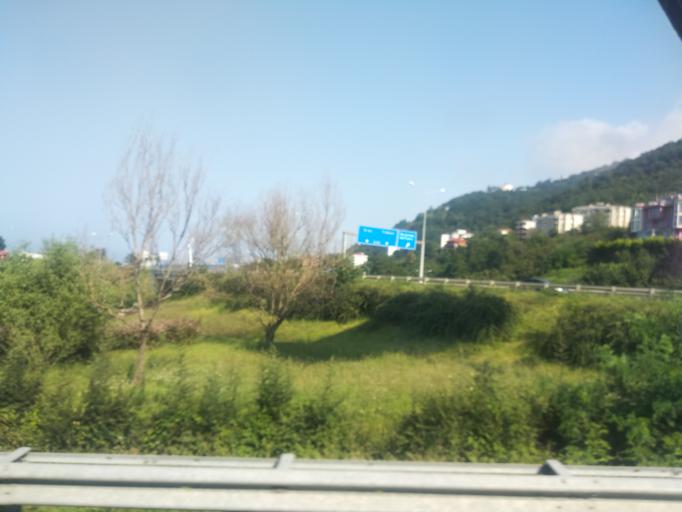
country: TR
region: Ordu
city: Ordu
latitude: 41.0170
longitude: 37.8438
